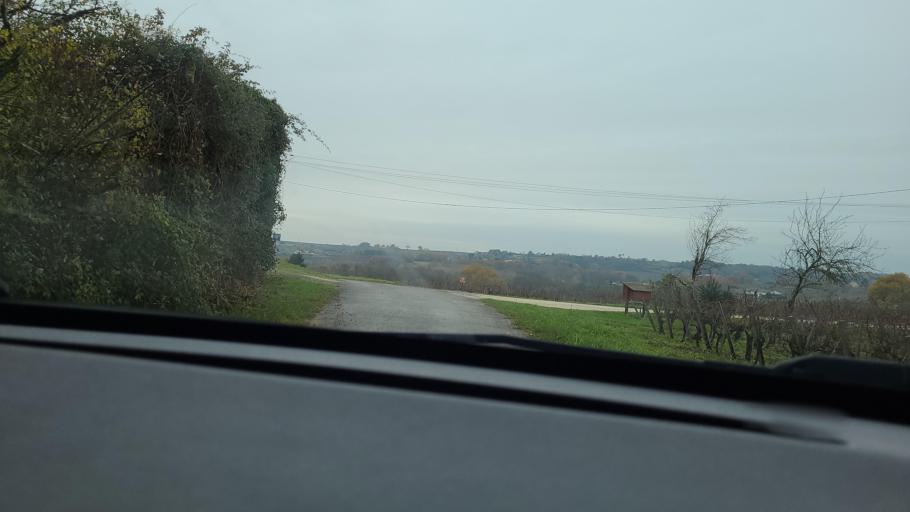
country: FR
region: Aquitaine
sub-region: Departement de la Gironde
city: Bourg
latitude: 45.0661
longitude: -0.5398
